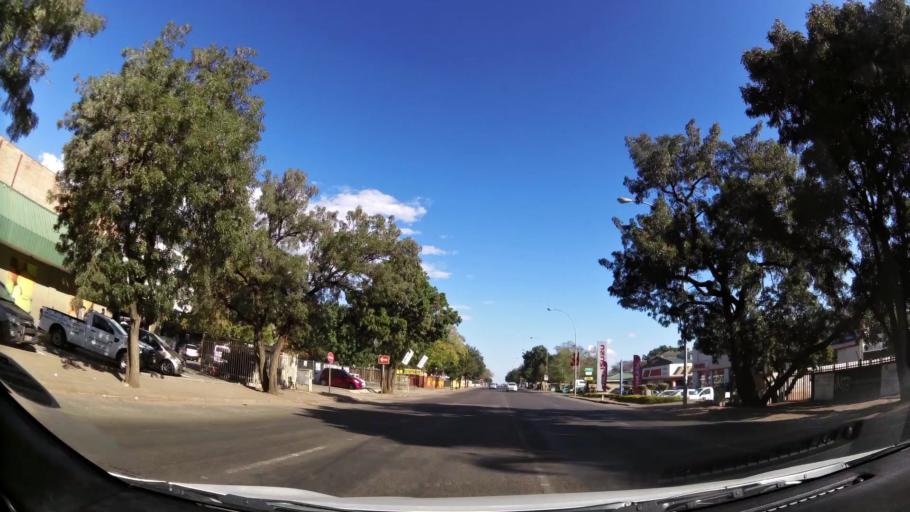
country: ZA
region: Limpopo
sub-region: Waterberg District Municipality
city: Mokopane
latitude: -24.1752
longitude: 29.0160
